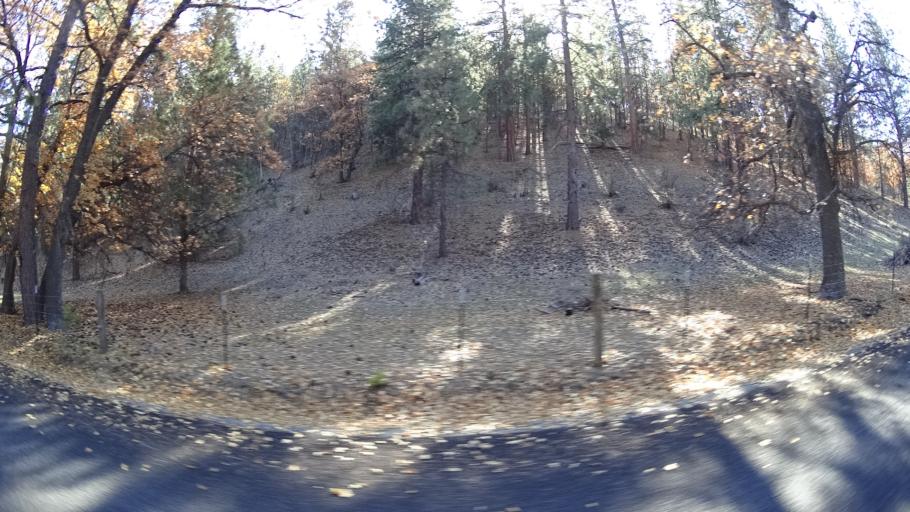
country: US
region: California
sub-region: Siskiyou County
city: Weed
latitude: 41.5035
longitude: -122.5822
